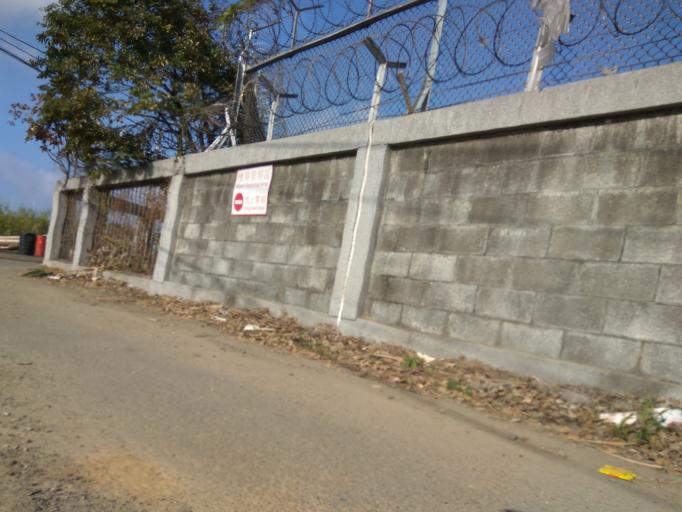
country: TW
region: Taiwan
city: Taoyuan City
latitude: 25.0553
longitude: 121.2158
